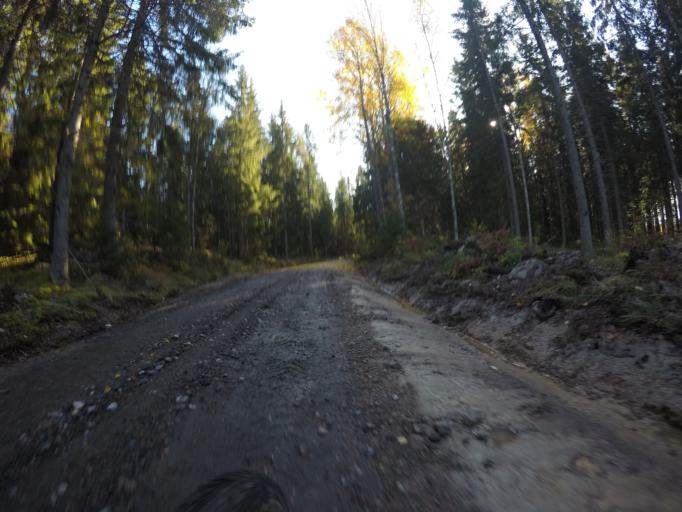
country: SE
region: Vaestmanland
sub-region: Kungsors Kommun
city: Kungsoer
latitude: 59.3102
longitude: 16.0994
